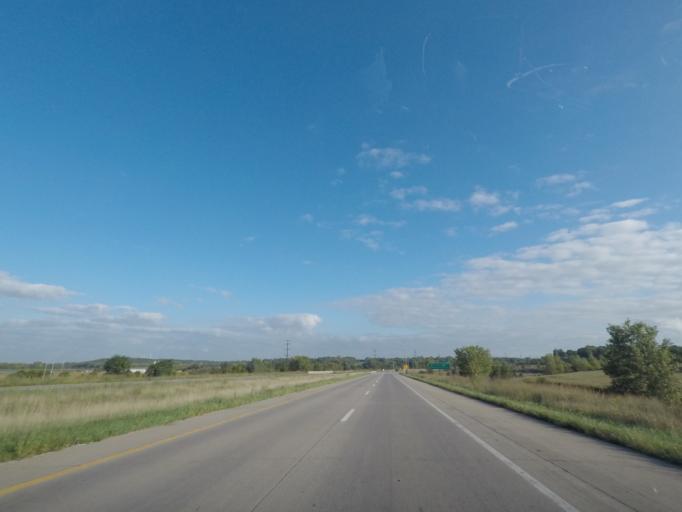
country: US
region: Iowa
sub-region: Polk County
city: Pleasant Hill
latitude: 41.5704
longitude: -93.5128
